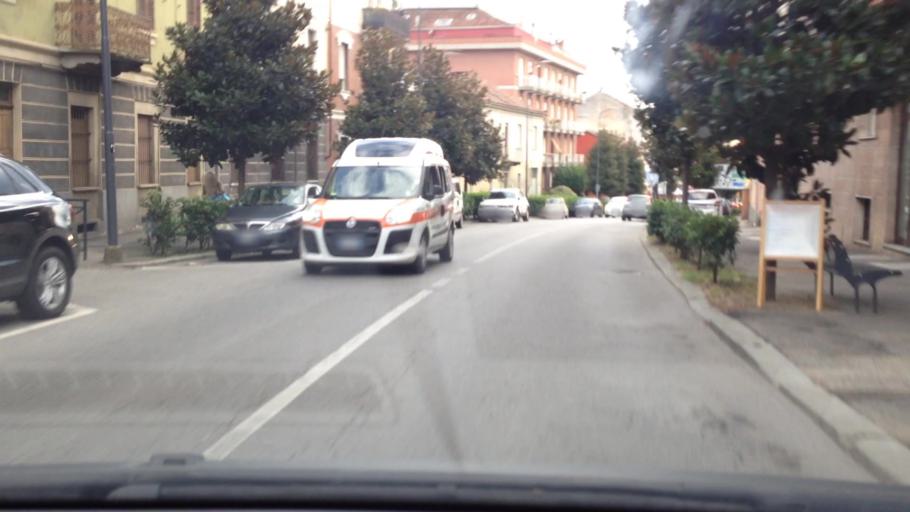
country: IT
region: Piedmont
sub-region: Provincia di Asti
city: Asti
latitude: 44.9013
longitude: 8.1954
